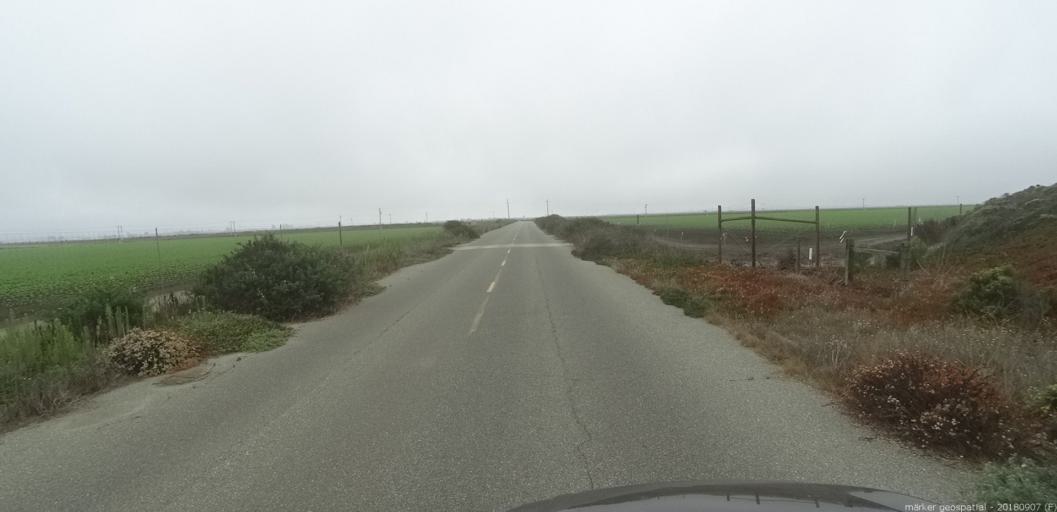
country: US
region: California
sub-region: Monterey County
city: Castroville
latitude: 36.7740
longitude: -121.7926
